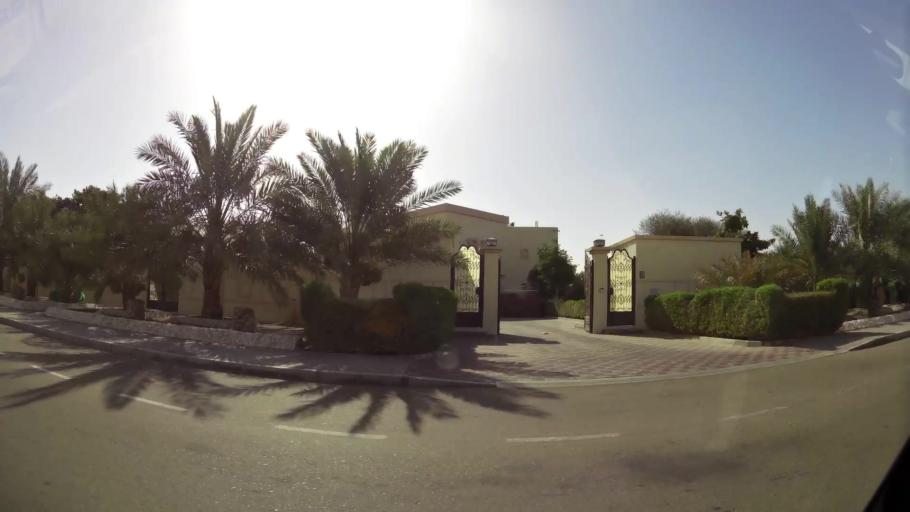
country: OM
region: Al Buraimi
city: Al Buraymi
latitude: 24.3403
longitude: 55.7829
